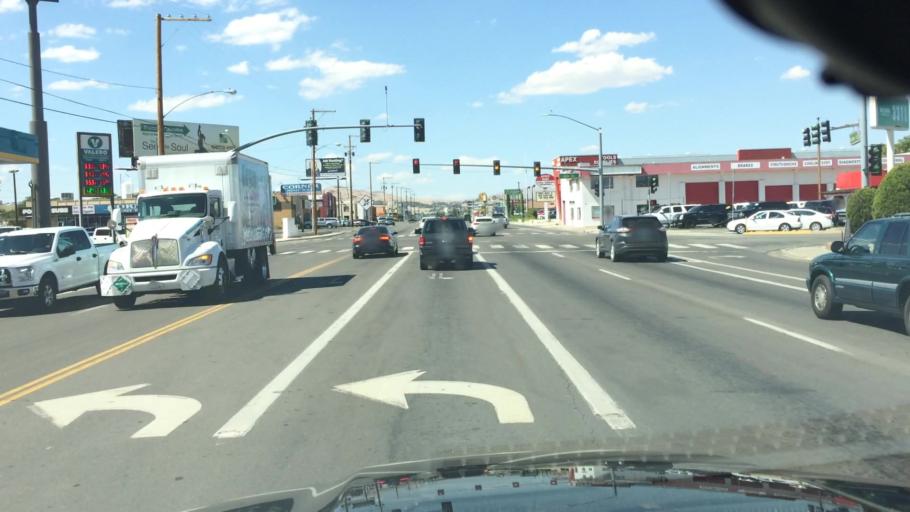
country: US
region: Nevada
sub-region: Washoe County
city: Reno
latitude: 39.5214
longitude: -119.7892
